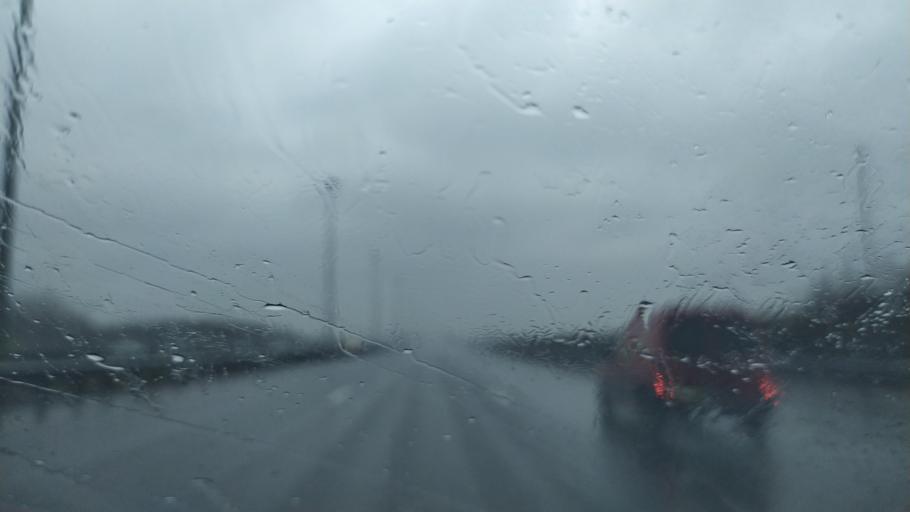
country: RU
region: Leningrad
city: Bugry
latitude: 60.0706
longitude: 30.3832
